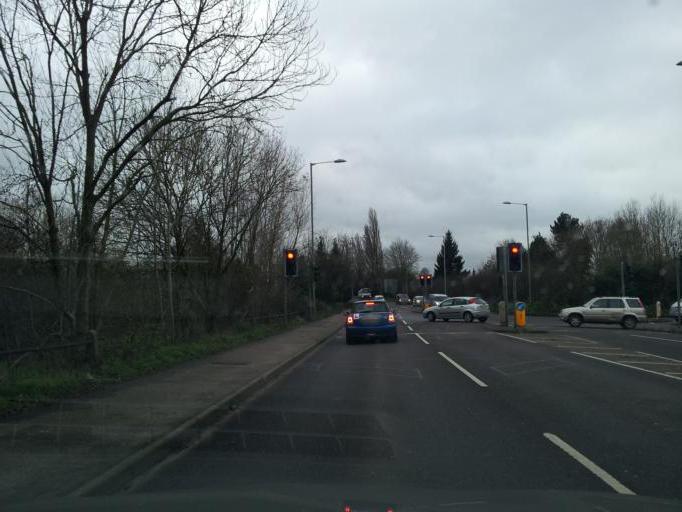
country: GB
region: England
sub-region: Norfolk
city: Cringleford
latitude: 52.5973
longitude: 1.2764
